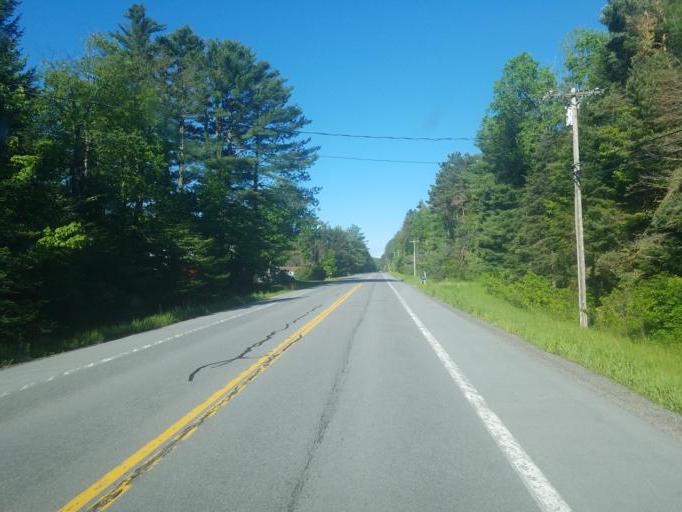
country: US
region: New York
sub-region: Oneida County
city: Utica
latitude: 43.3498
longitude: -75.0687
